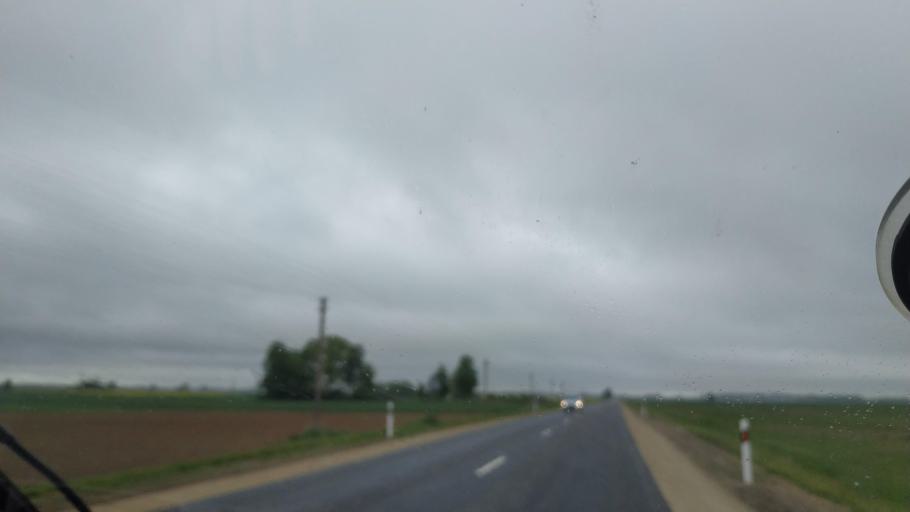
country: LT
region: Panevezys
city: Pasvalys
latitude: 56.0329
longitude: 24.4452
